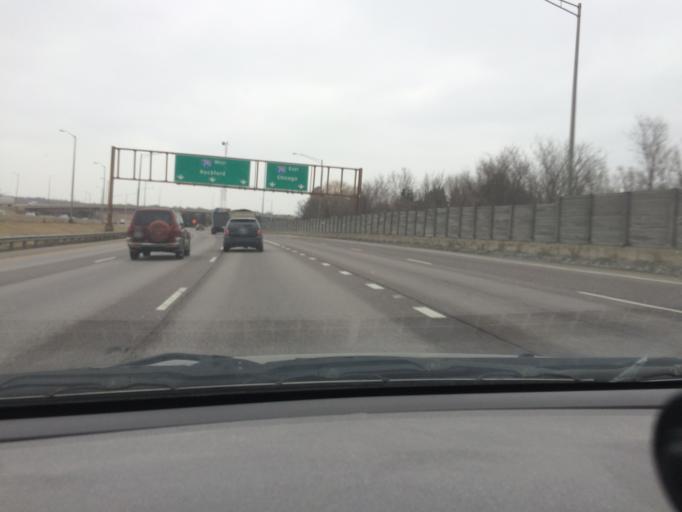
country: US
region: Illinois
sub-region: DuPage County
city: Itasca
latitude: 41.9552
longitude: -88.0292
